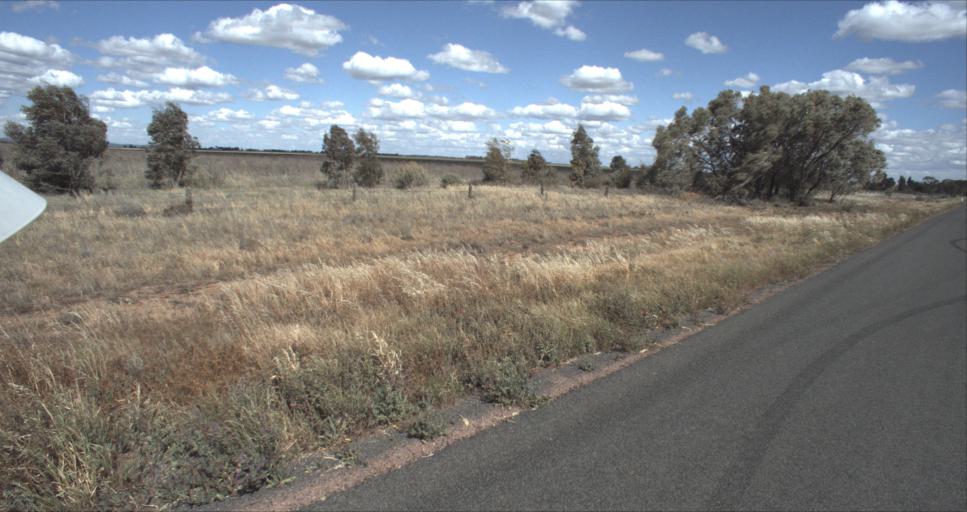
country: AU
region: New South Wales
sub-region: Leeton
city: Leeton
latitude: -34.4309
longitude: 146.2582
